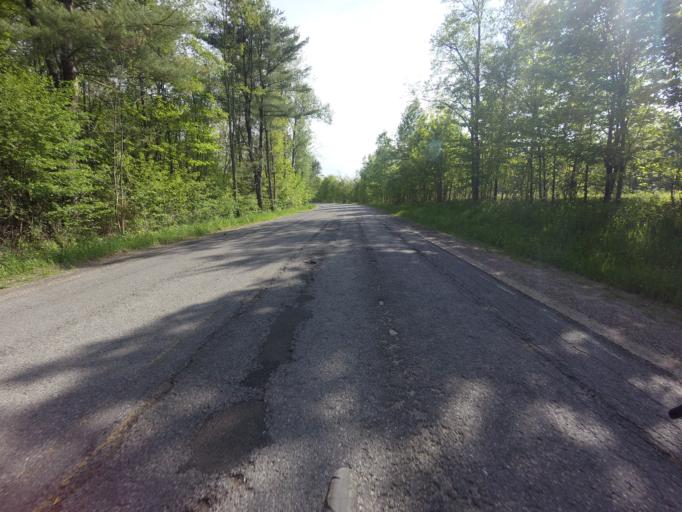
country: US
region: New York
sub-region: St. Lawrence County
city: Gouverneur
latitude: 44.2427
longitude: -75.2235
